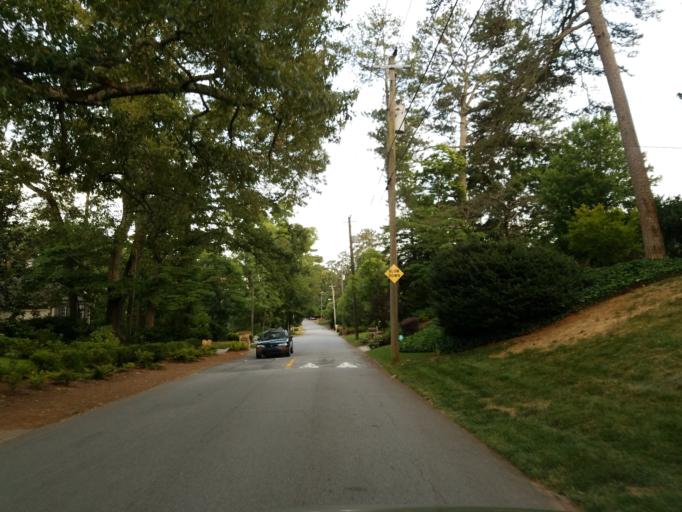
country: US
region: Georgia
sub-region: Fulton County
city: Sandy Springs
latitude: 33.8853
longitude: -84.3956
